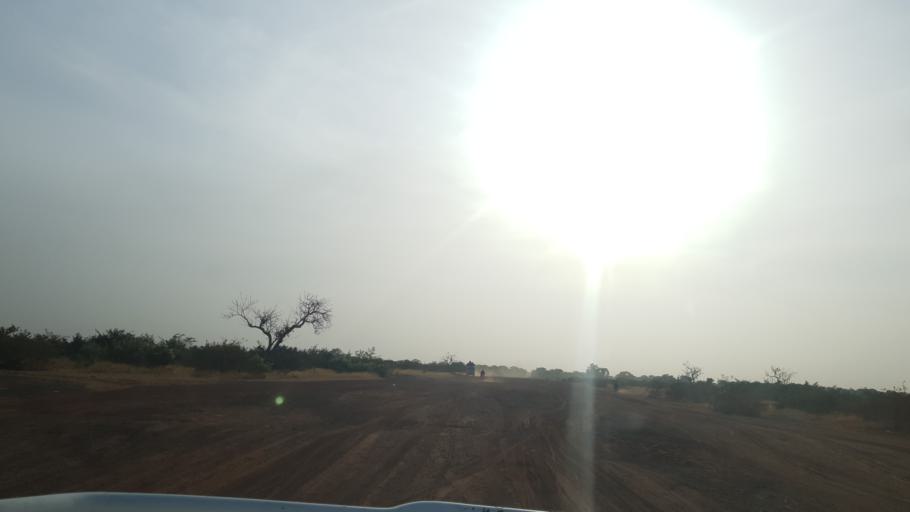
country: ML
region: Koulikoro
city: Dioila
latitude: 12.7654
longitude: -6.9165
